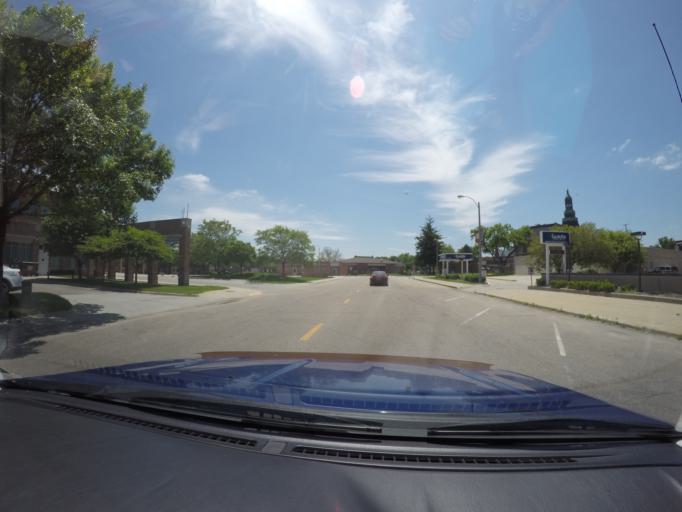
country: US
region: Nebraska
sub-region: Hall County
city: Grand Island
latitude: 40.9247
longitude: -98.3392
